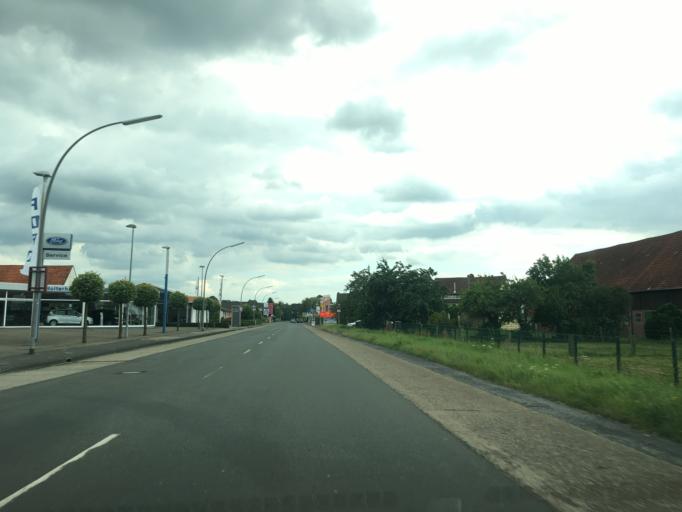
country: DE
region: North Rhine-Westphalia
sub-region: Regierungsbezirk Munster
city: Telgte
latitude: 51.9244
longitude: 7.7250
